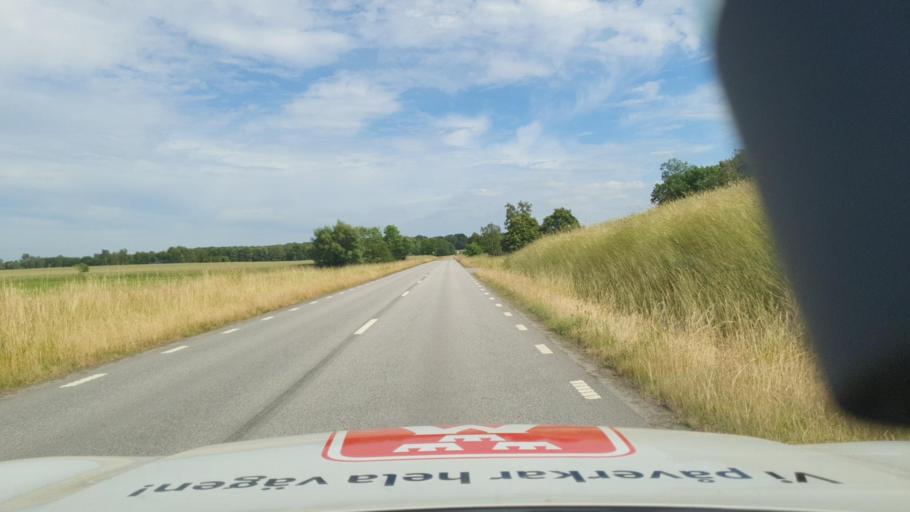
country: SE
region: Skane
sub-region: Sjobo Kommun
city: Blentarp
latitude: 55.6029
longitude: 13.5882
